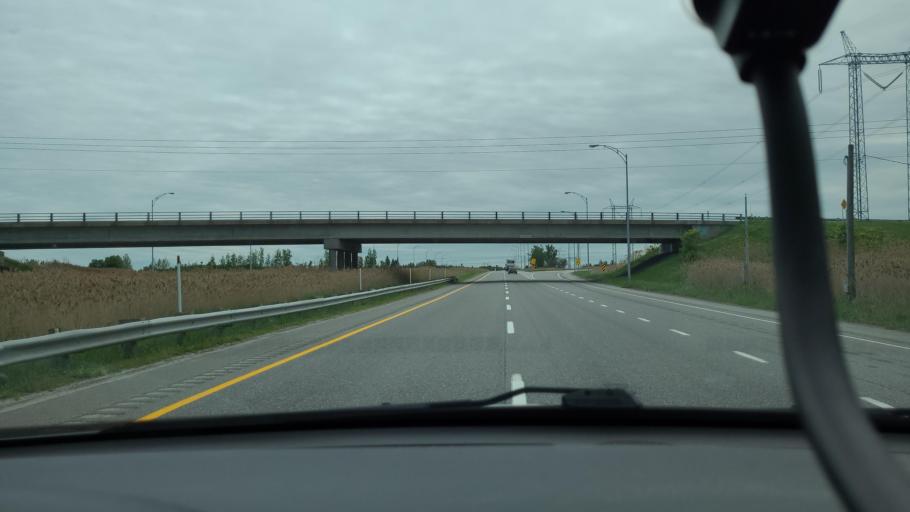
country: CA
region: Quebec
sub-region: Lanaudiere
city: Mascouche
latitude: 45.7907
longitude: -73.5807
